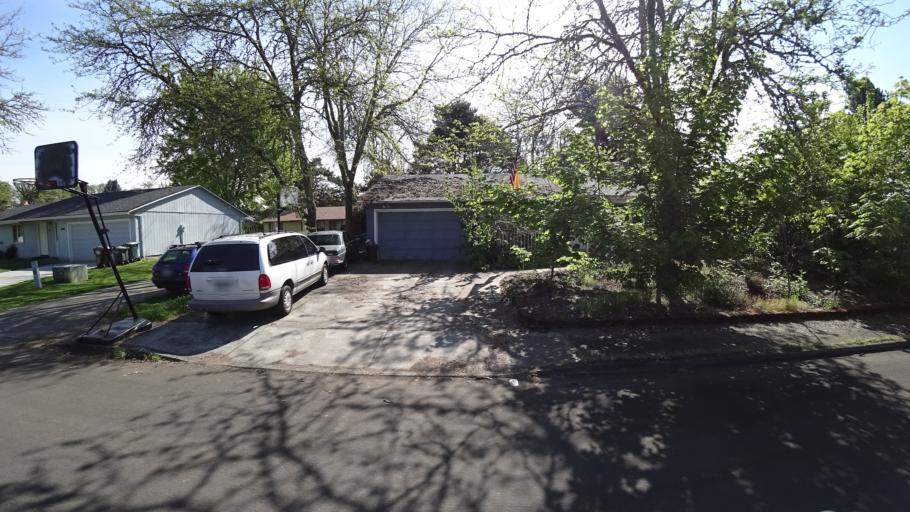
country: US
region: Oregon
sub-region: Washington County
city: Hillsboro
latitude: 45.5238
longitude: -122.9471
